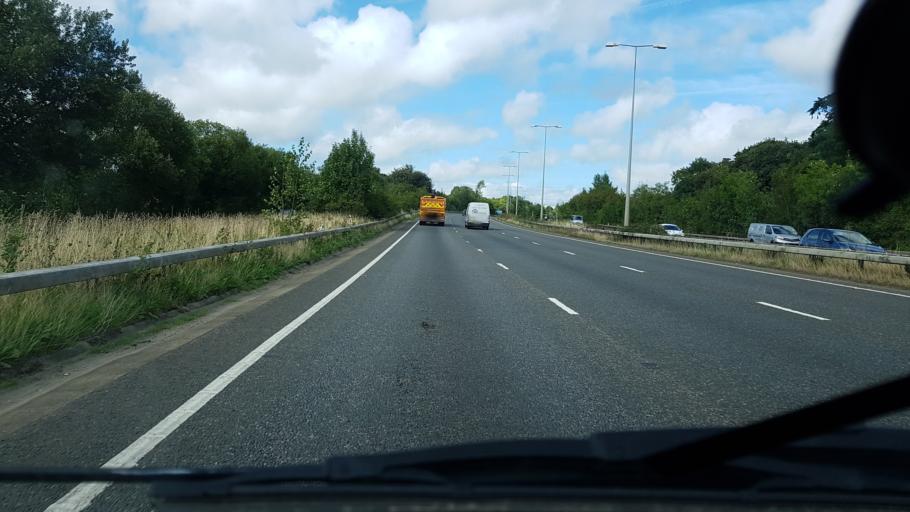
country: GB
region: England
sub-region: West Sussex
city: Broadfield
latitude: 51.0767
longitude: -0.2037
